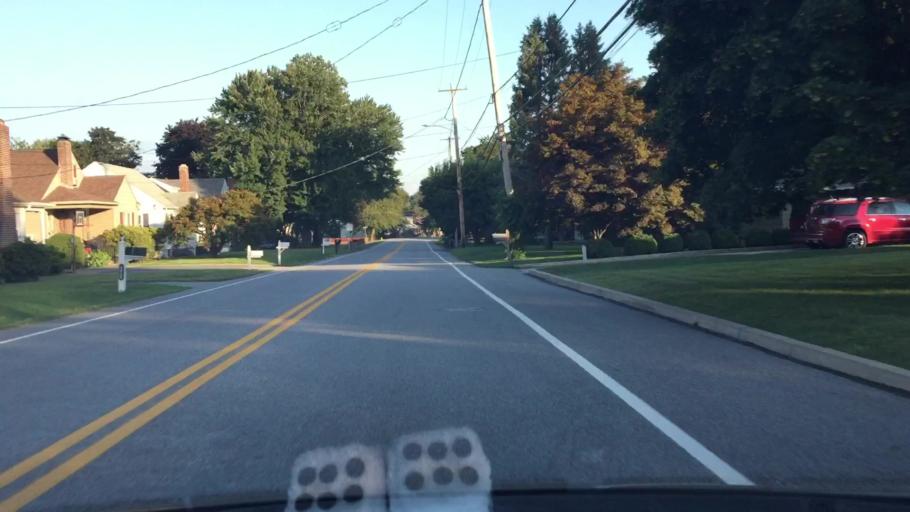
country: US
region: Pennsylvania
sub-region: Delaware County
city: Boothwyn
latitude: 39.8262
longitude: -75.4510
